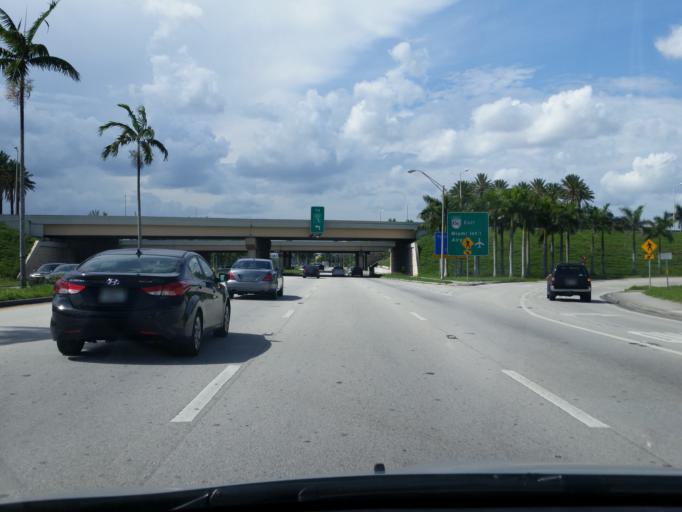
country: US
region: Florida
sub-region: Miami-Dade County
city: Sweetwater
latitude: 25.7791
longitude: -80.3691
